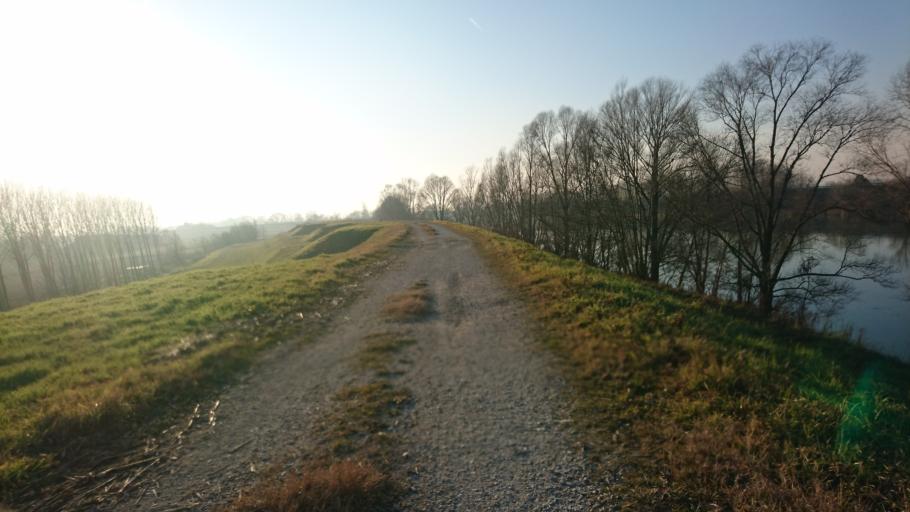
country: IT
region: Veneto
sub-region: Provincia di Rovigo
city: Mardimago
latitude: 45.1226
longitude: 11.8144
